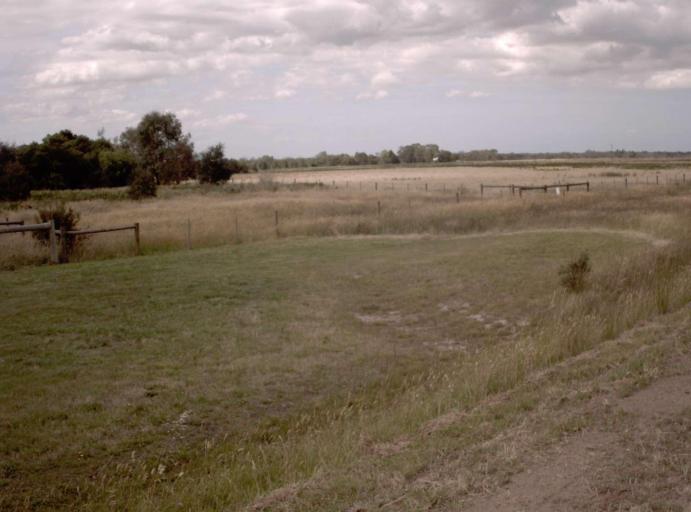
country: AU
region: Victoria
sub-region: Wellington
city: Sale
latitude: -38.1656
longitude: 147.0423
